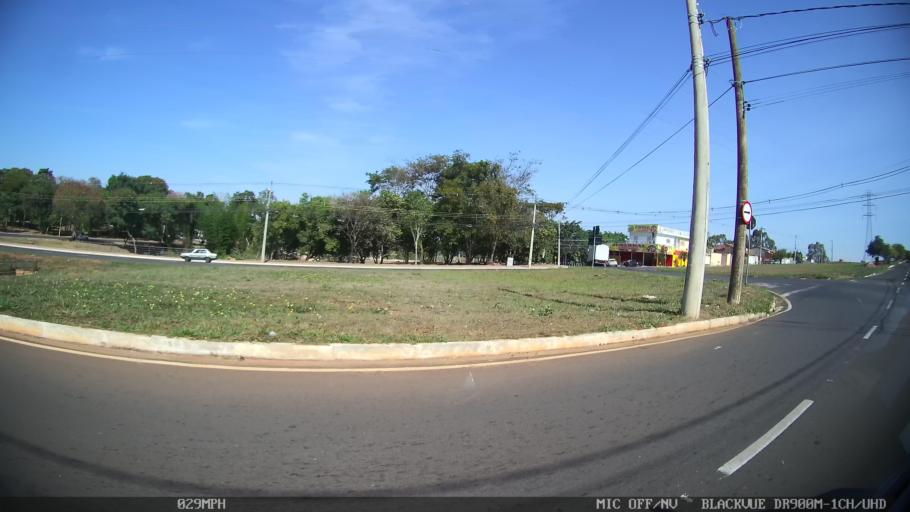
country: BR
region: Sao Paulo
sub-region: Sao Jose Do Rio Preto
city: Sao Jose do Rio Preto
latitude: -20.7933
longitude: -49.4258
